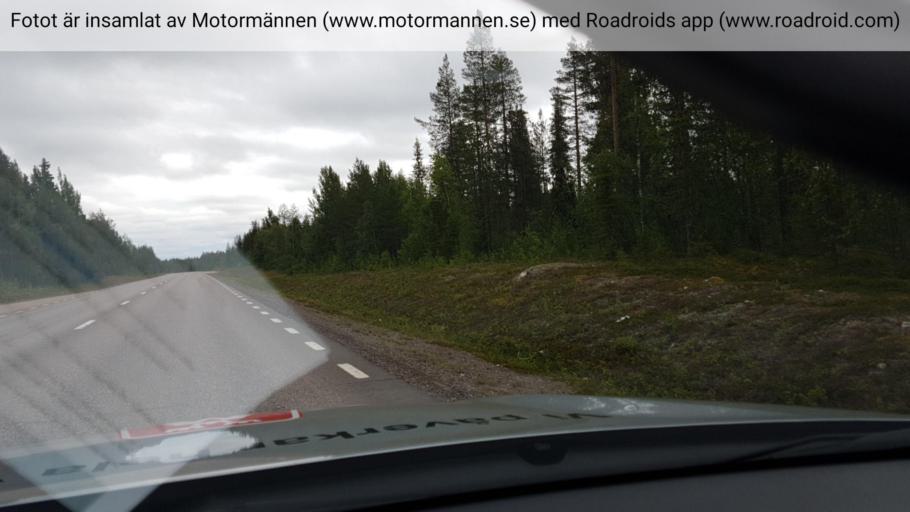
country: SE
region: Norrbotten
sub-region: Gallivare Kommun
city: Gaellivare
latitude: 67.0707
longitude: 21.1111
